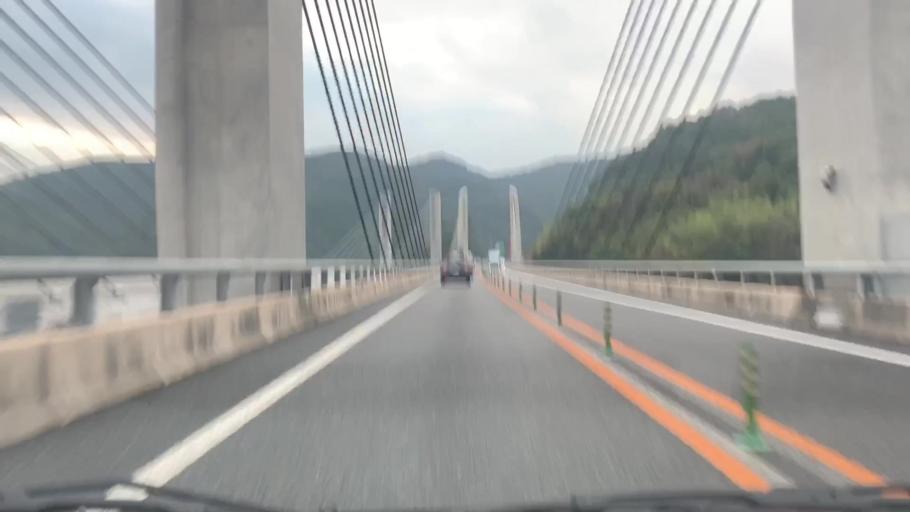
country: JP
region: Nagasaki
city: Nagasaki-shi
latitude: 32.7585
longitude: 129.9290
